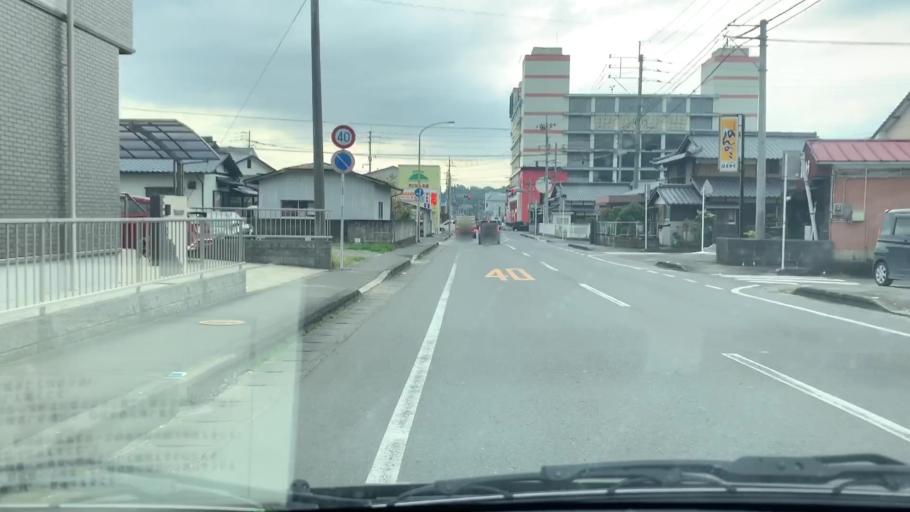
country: JP
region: Saga Prefecture
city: Takeocho-takeo
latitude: 33.1975
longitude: 130.0268
